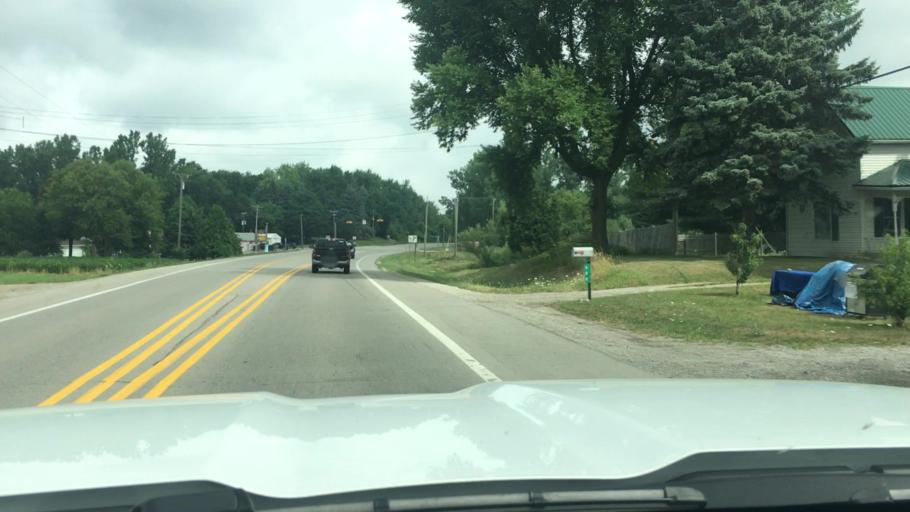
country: US
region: Michigan
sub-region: Lapeer County
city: Imlay City
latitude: 43.0640
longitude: -83.0735
